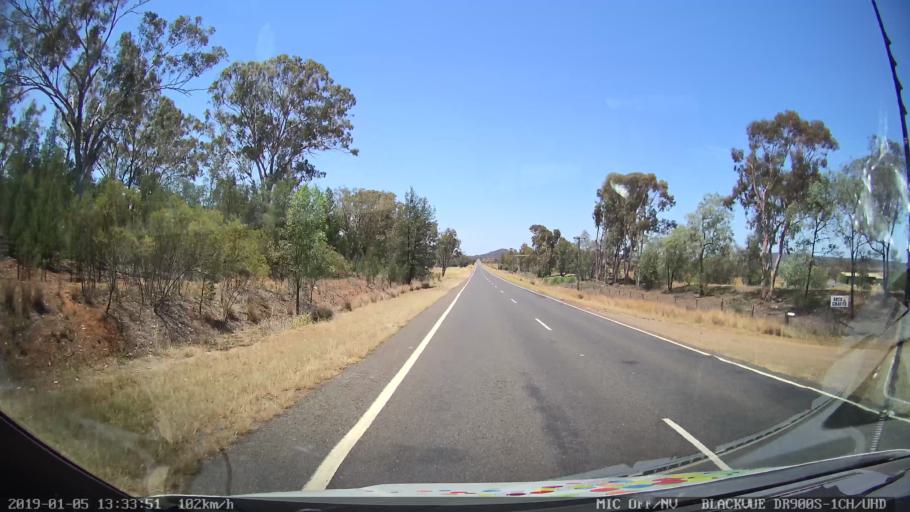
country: AU
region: New South Wales
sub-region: Gunnedah
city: Gunnedah
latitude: -30.9987
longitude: 150.1232
